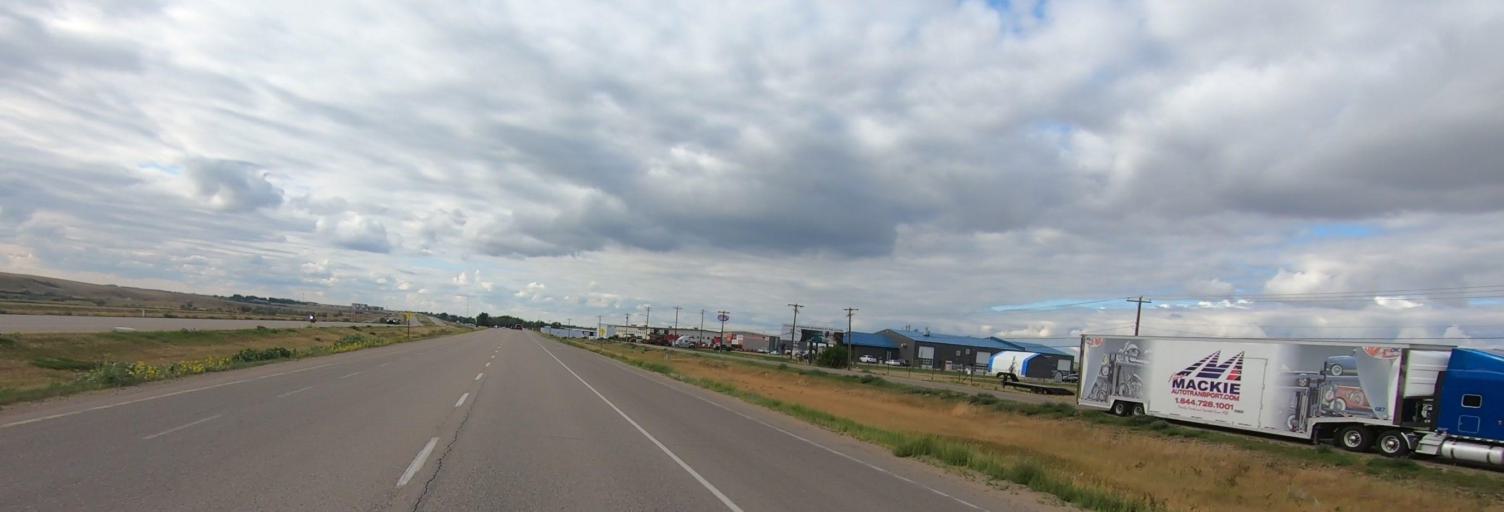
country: CA
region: Alberta
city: Medicine Hat
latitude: 49.9744
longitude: -110.6060
